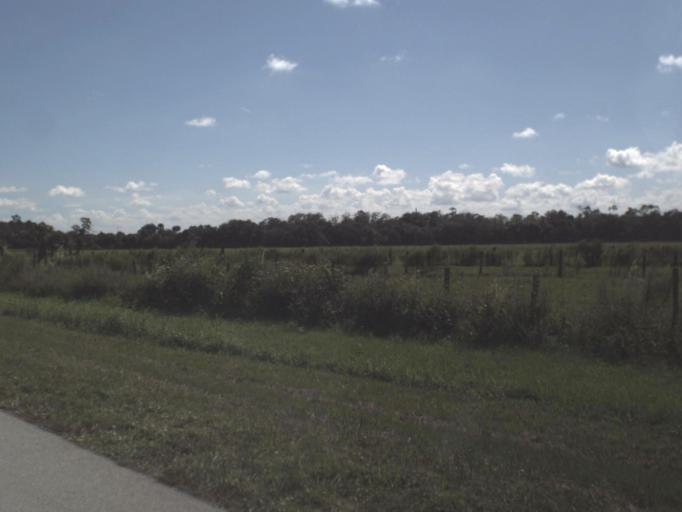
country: US
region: Florida
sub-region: Hendry County
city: Port LaBelle
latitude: 26.8126
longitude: -81.3658
